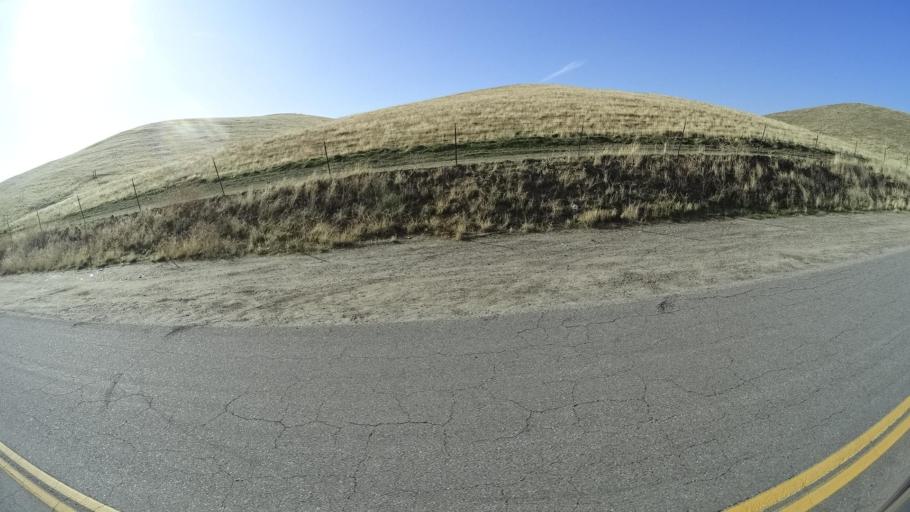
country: US
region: California
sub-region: Kern County
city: Bear Valley Springs
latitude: 35.2755
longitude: -118.6893
